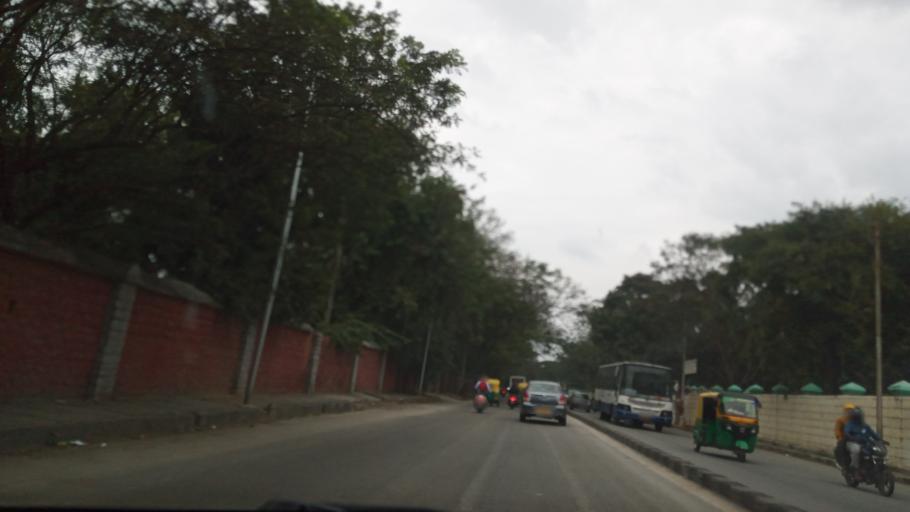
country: IN
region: Karnataka
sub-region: Bangalore Urban
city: Bangalore
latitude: 13.0021
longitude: 77.5943
